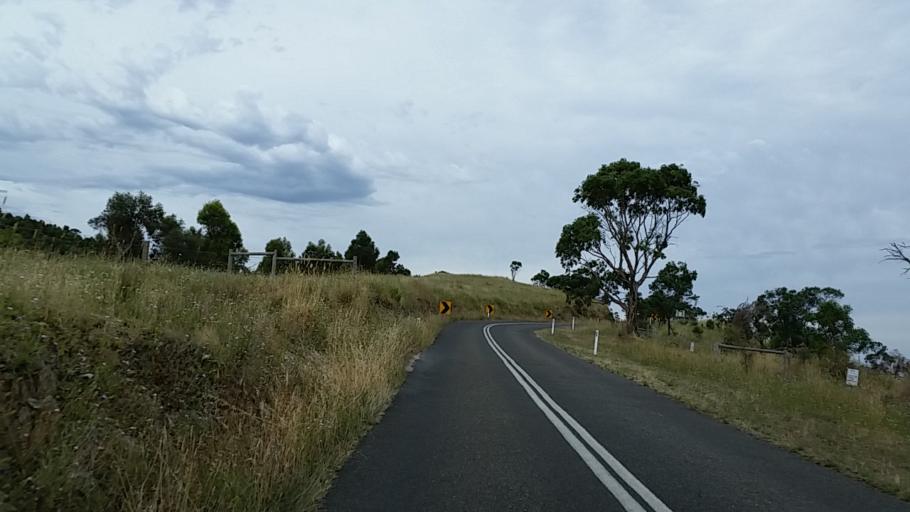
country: AU
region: South Australia
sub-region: Yankalilla
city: Normanville
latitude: -35.3989
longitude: 138.4193
